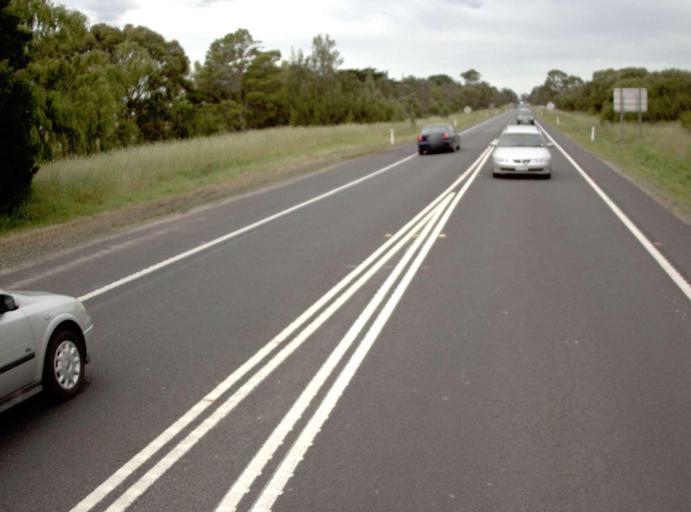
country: AU
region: Victoria
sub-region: Wellington
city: Sale
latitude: -38.0697
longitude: 147.0736
